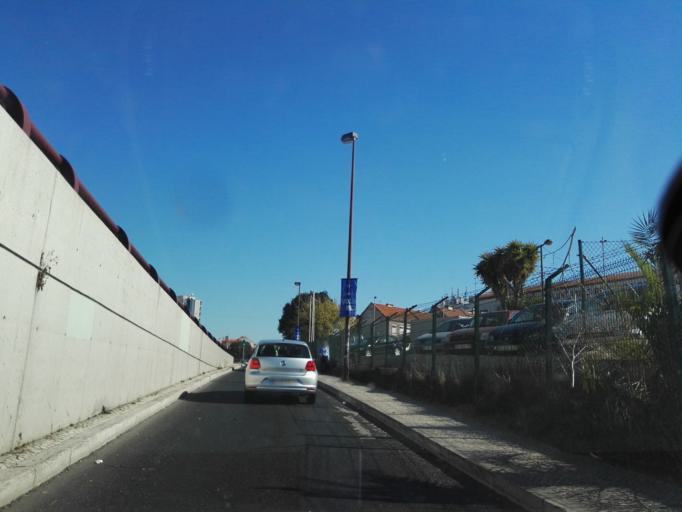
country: PT
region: Lisbon
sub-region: Lisbon
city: Lisbon
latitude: 38.7225
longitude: -9.1655
